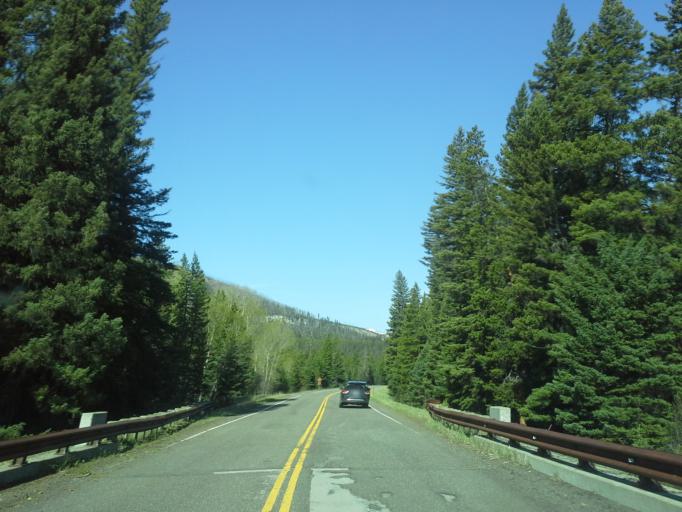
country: US
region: Montana
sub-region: Carbon County
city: Red Lodge
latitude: 44.9578
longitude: -109.8058
